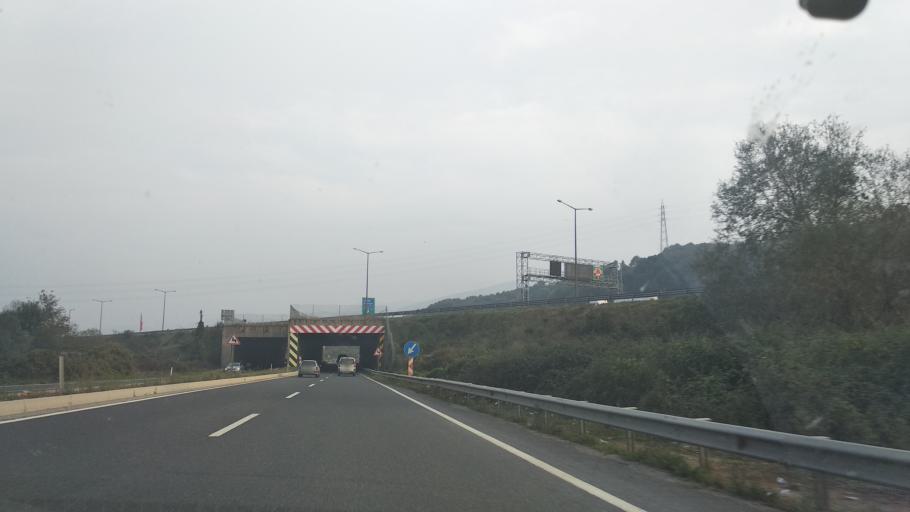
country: TR
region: Duzce
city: Kaynasli
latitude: 40.7864
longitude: 31.2646
